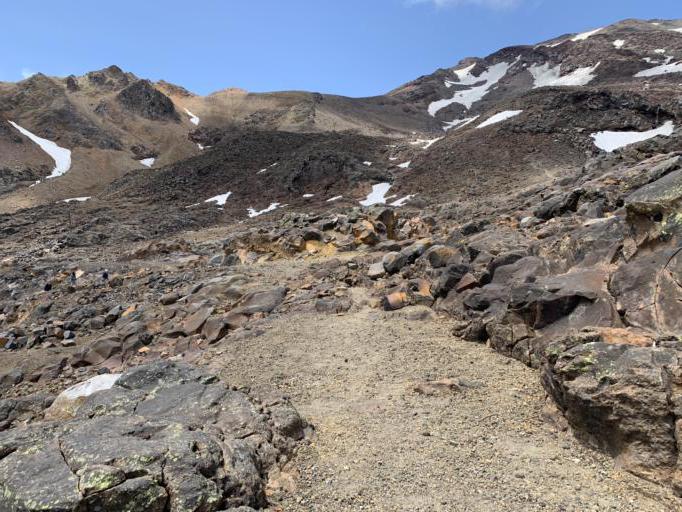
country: NZ
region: Manawatu-Wanganui
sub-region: Ruapehu District
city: Waiouru
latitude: -39.2527
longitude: 175.5636
